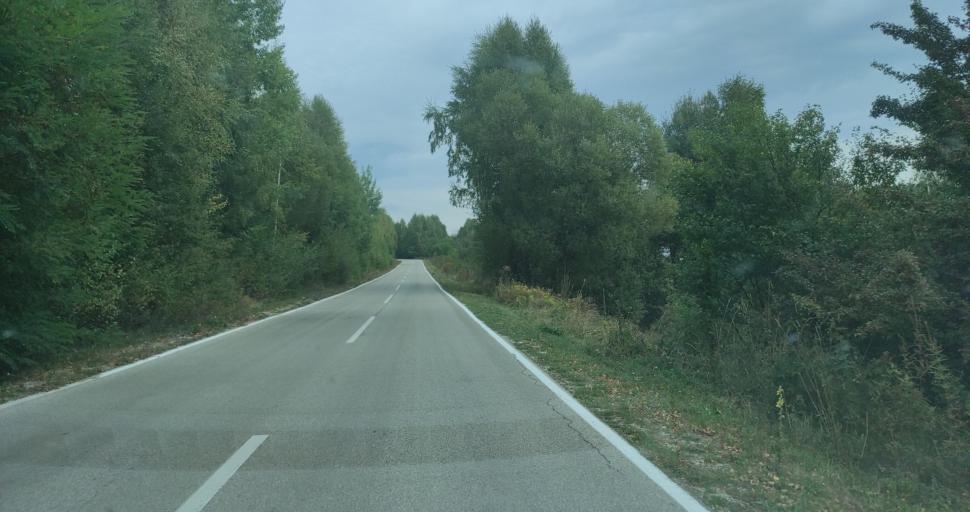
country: RS
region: Central Serbia
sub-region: Jablanicki Okrug
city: Crna Trava
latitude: 42.7186
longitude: 22.3321
